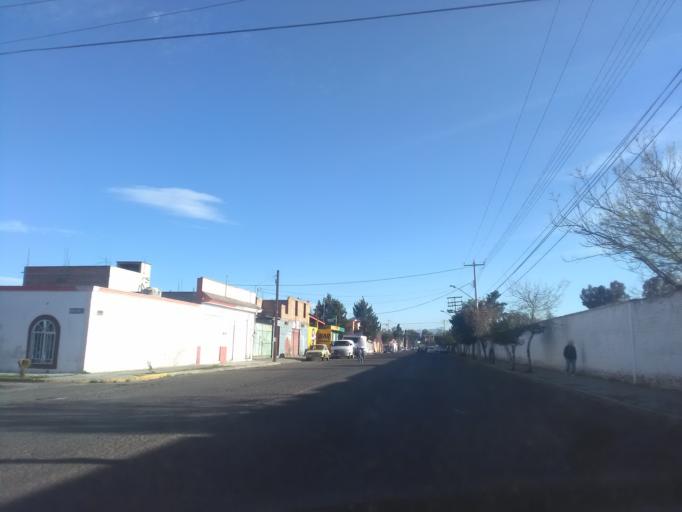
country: MX
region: Durango
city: Victoria de Durango
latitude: 24.0301
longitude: -104.6345
